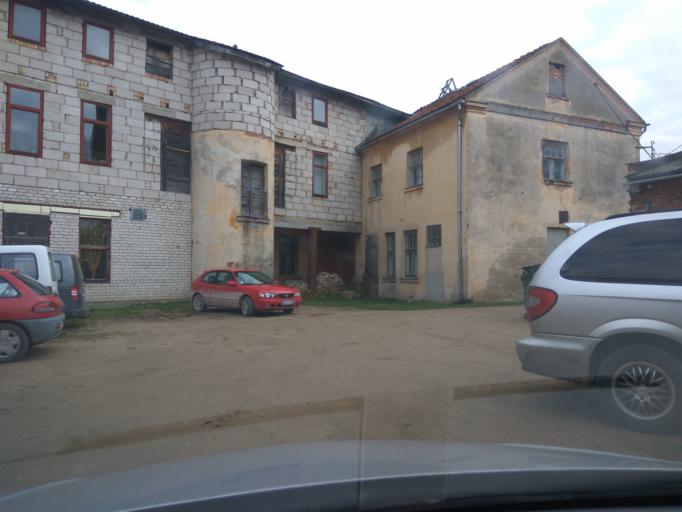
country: LV
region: Kuldigas Rajons
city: Kuldiga
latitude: 56.9662
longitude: 21.9699
